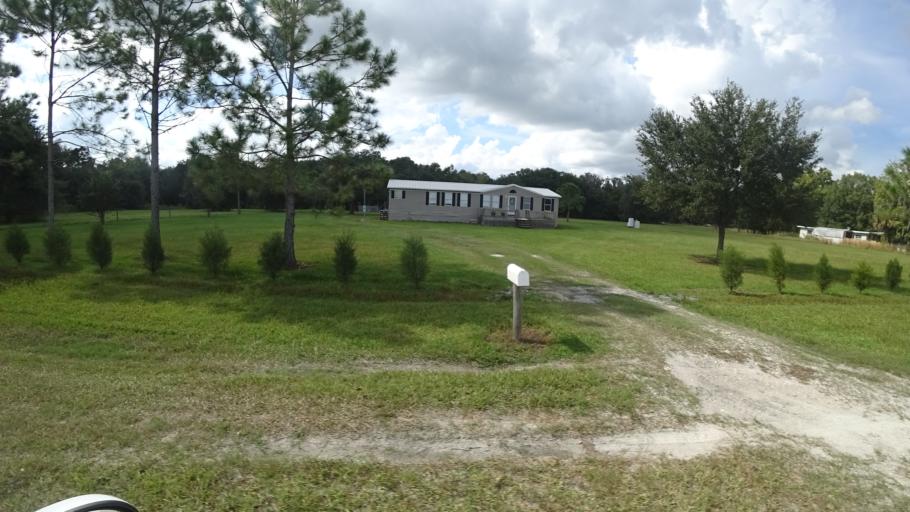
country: US
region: Florida
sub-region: Hillsborough County
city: Wimauma
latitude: 27.5473
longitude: -82.1745
